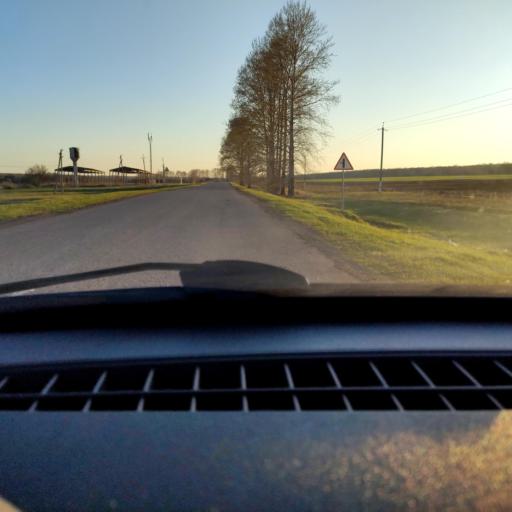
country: RU
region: Bashkortostan
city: Avdon
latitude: 54.4867
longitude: 55.5863
